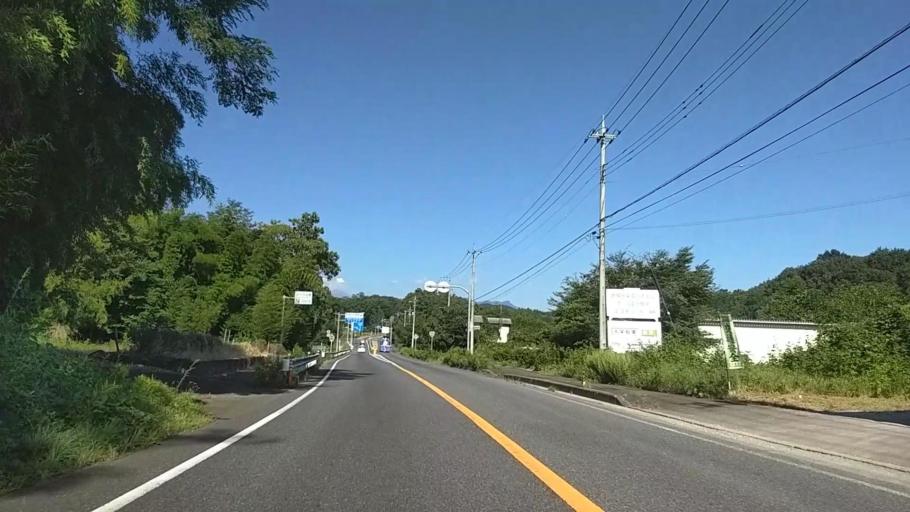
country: JP
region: Gunma
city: Annaka
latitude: 36.3074
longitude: 138.8209
